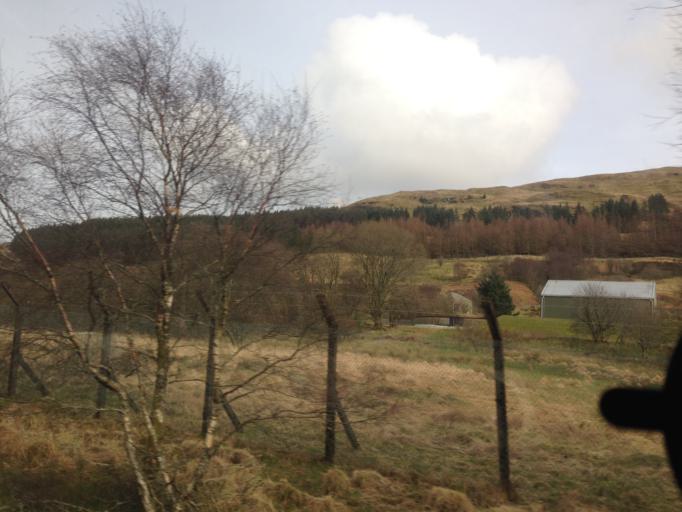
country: GB
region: Scotland
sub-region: Argyll and Bute
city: Garelochhead
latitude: 56.1503
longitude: -4.7826
